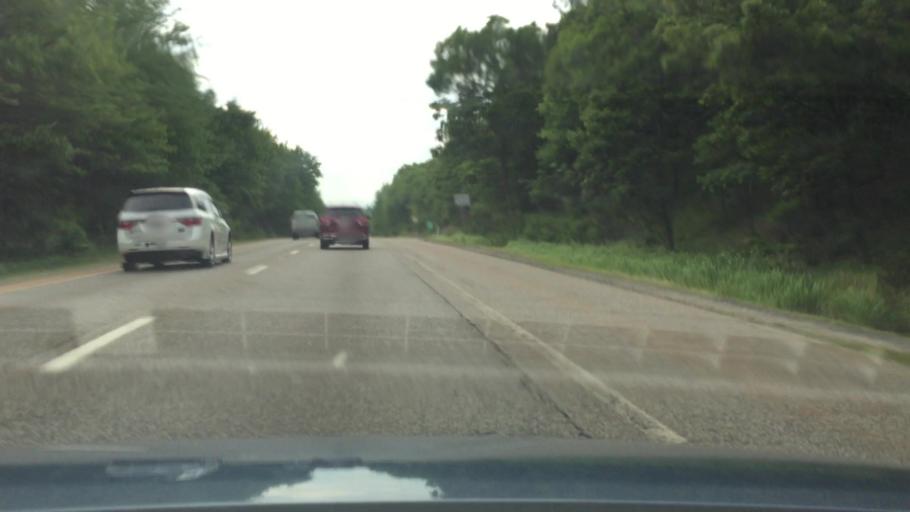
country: US
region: Massachusetts
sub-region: Plymouth County
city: Hanover
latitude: 42.1220
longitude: -70.7893
